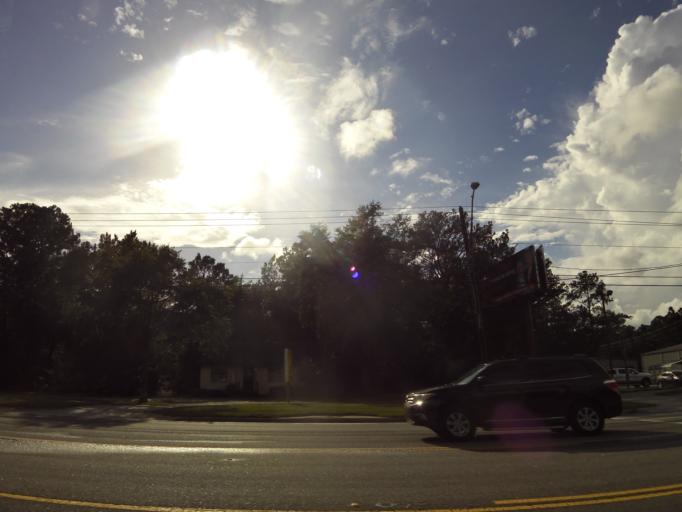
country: US
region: Georgia
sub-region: Liberty County
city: Hinesville
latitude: 31.8501
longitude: -81.6059
